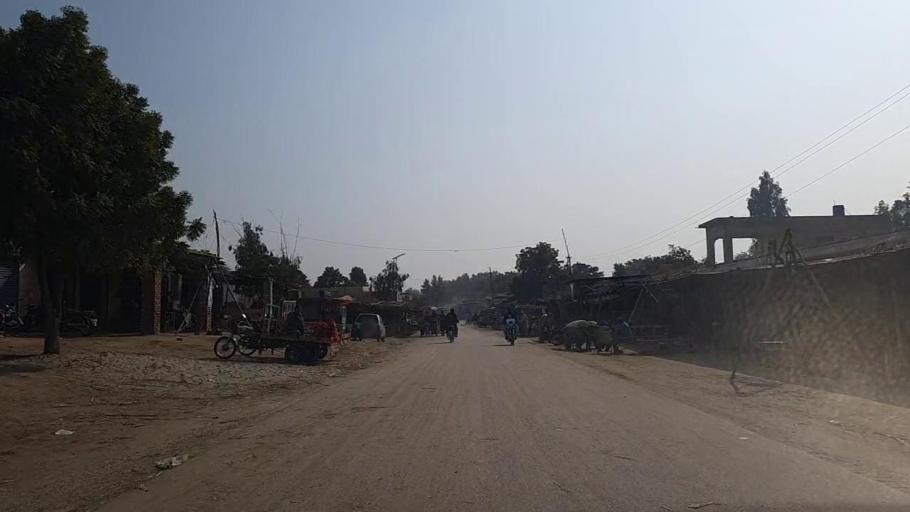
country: PK
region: Sindh
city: Jam Sahib
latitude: 26.3322
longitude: 68.5373
